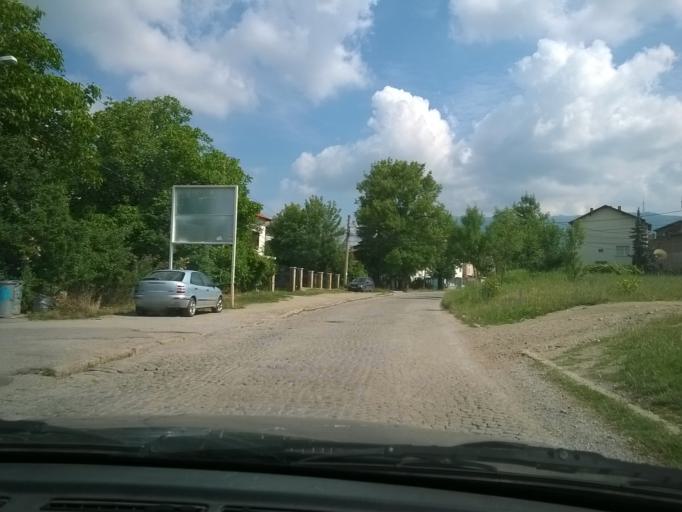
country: BG
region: Sofiya
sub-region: Obshtina Bozhurishte
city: Bozhurishte
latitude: 42.6806
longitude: 23.2405
